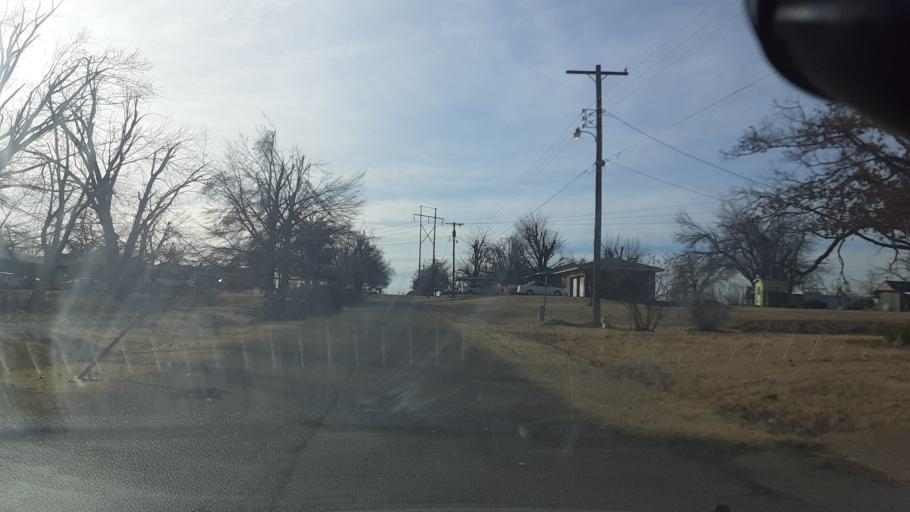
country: US
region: Oklahoma
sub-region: Logan County
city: Guthrie
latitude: 35.8552
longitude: -97.4331
